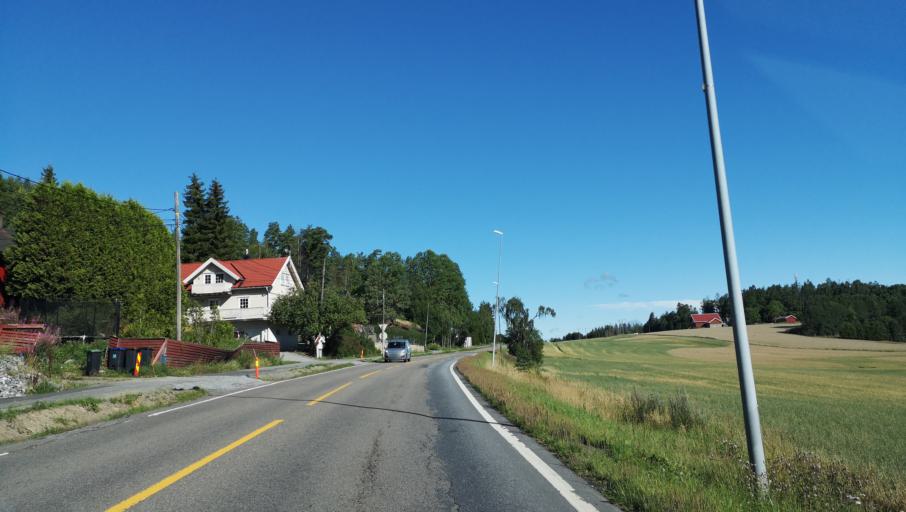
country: NO
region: Ostfold
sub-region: Spydeberg
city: Spydeberg
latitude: 59.5898
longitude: 11.1122
